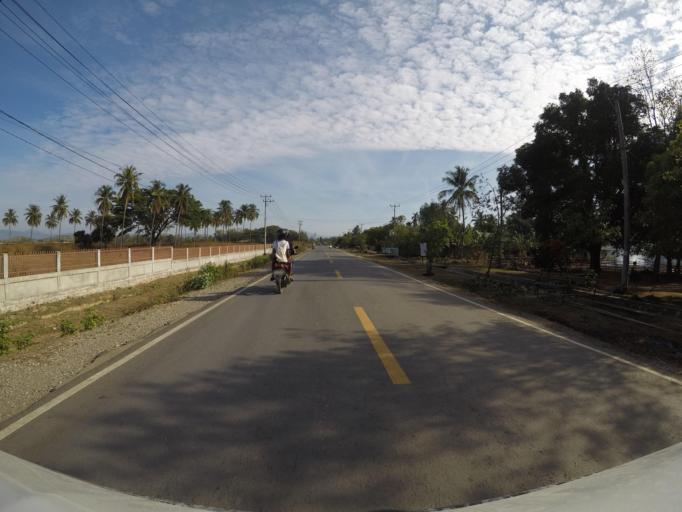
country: TL
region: Bobonaro
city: Maliana
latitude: -8.9758
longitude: 125.2197
